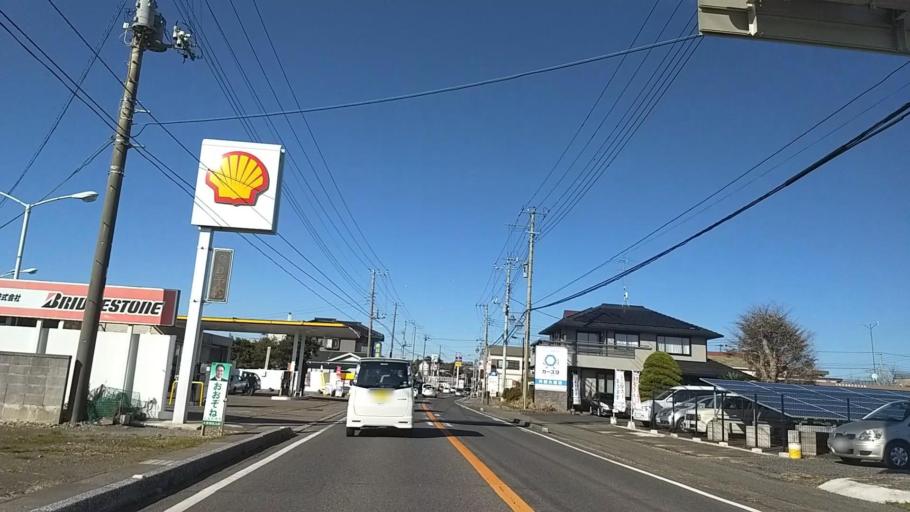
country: JP
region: Chiba
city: Ohara
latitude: 35.2568
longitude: 140.3941
